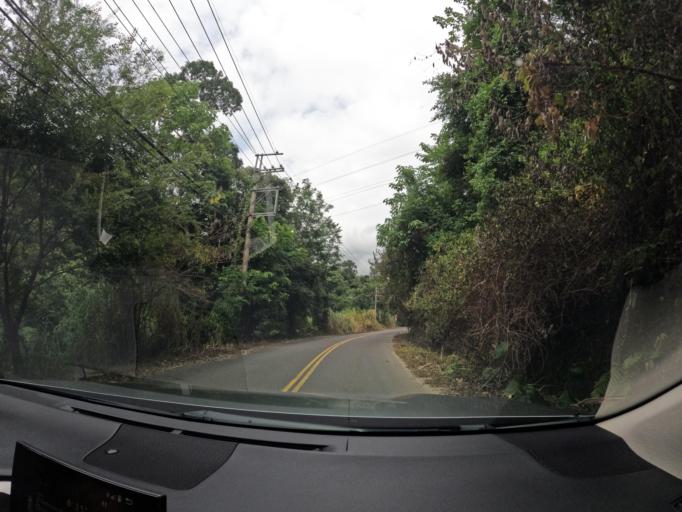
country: TW
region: Taiwan
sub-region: Miaoli
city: Miaoli
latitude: 24.3804
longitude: 120.8647
